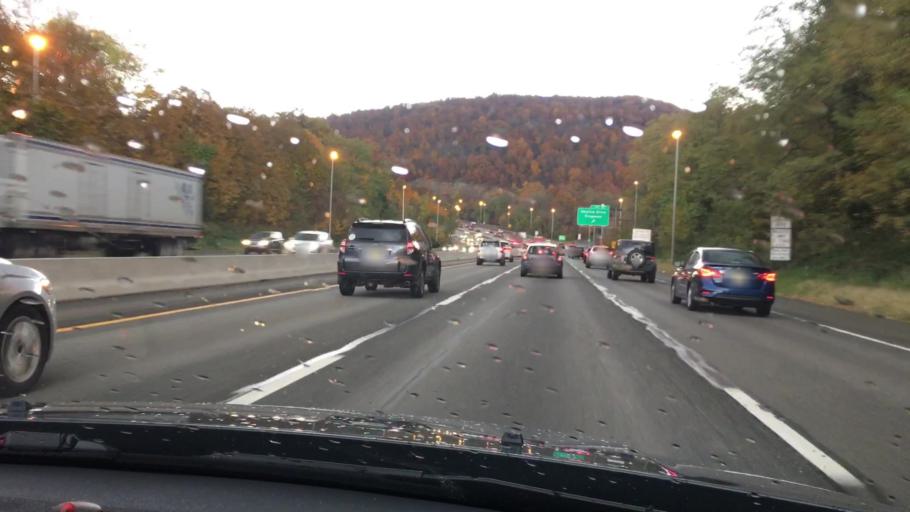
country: US
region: New Jersey
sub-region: Bergen County
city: Oakland
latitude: 41.0285
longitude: -74.2447
